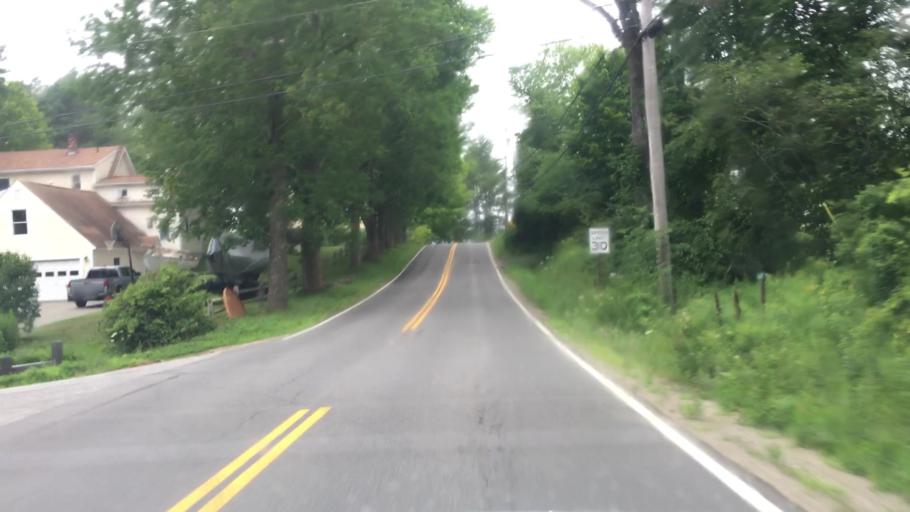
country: US
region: Maine
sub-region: Lincoln County
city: Wiscasset
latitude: 43.9889
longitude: -69.6487
